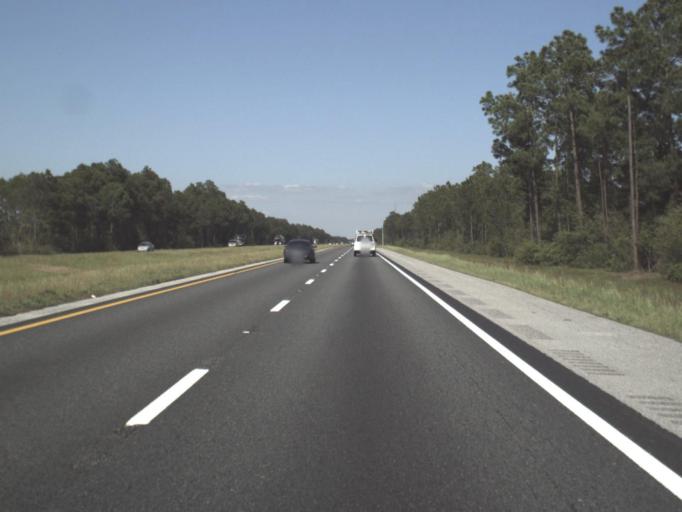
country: US
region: Florida
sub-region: Santa Rosa County
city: Bagdad
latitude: 30.5451
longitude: -87.0634
